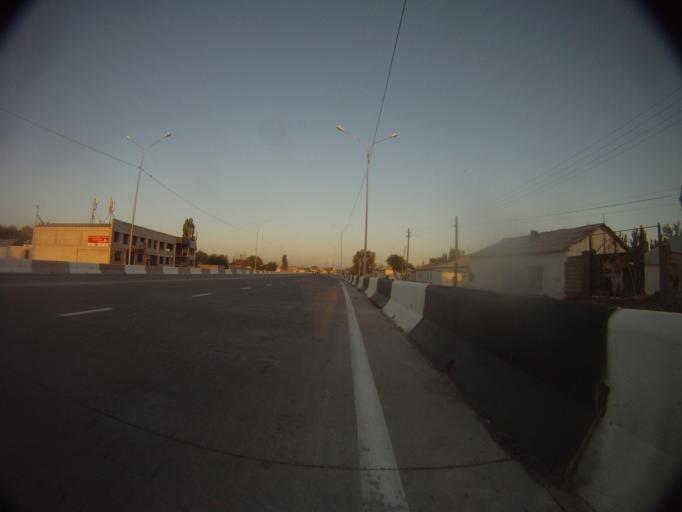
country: KZ
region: Ongtustik Qazaqstan
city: Turkestan
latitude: 43.2598
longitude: 68.3784
